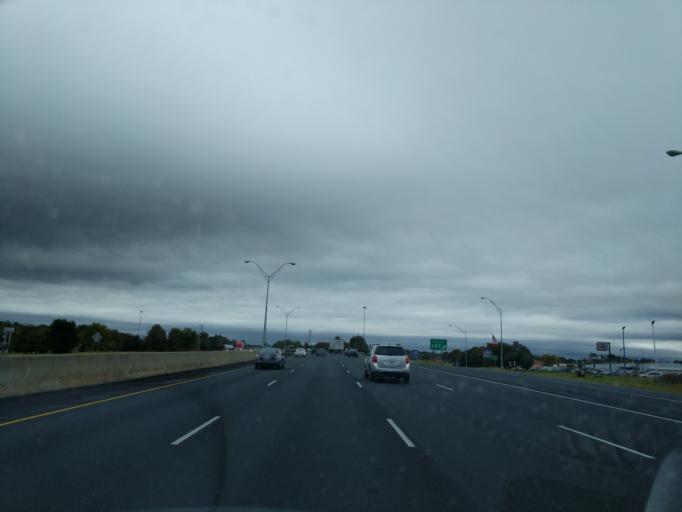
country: US
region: North Carolina
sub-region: Alamance County
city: Graham
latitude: 36.0603
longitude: -79.4038
